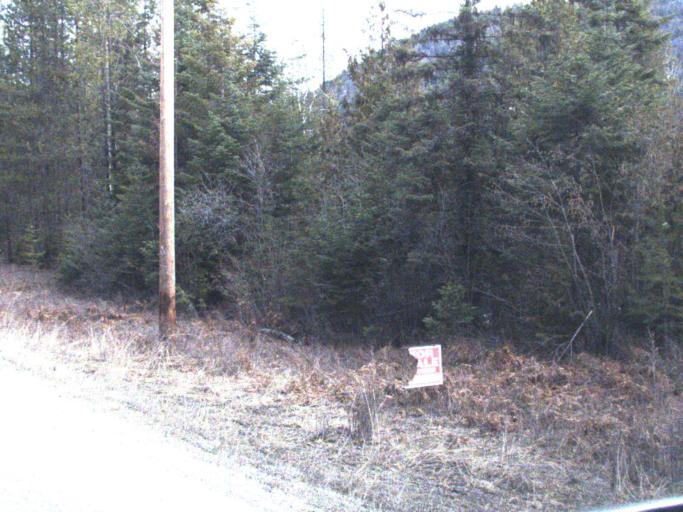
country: US
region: Washington
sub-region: Stevens County
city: Chewelah
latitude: 48.5859
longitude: -117.3520
